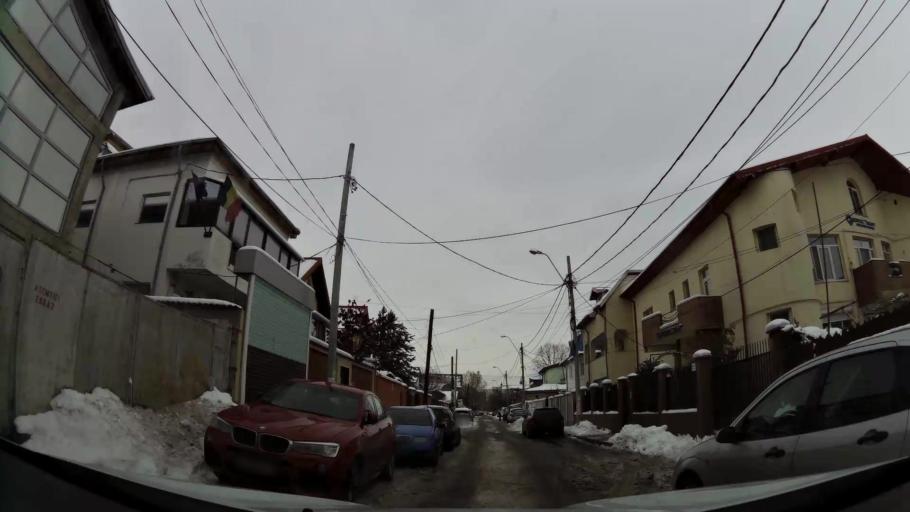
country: RO
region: Bucuresti
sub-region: Municipiul Bucuresti
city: Bucuresti
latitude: 44.3891
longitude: 26.1045
